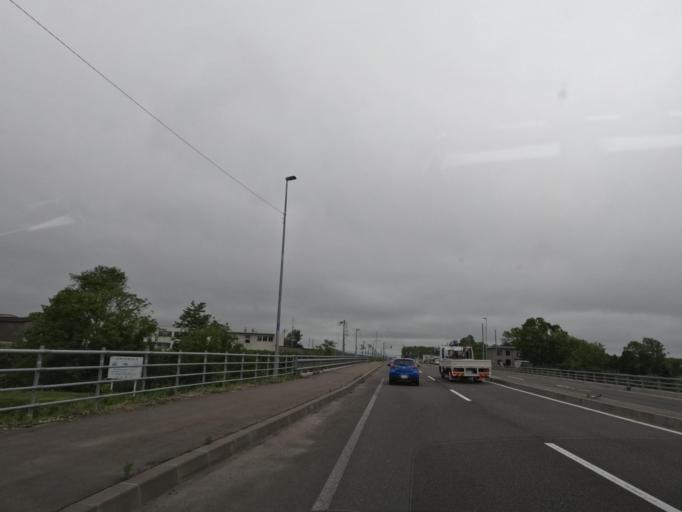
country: JP
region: Hokkaido
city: Ebetsu
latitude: 43.1465
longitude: 141.5171
